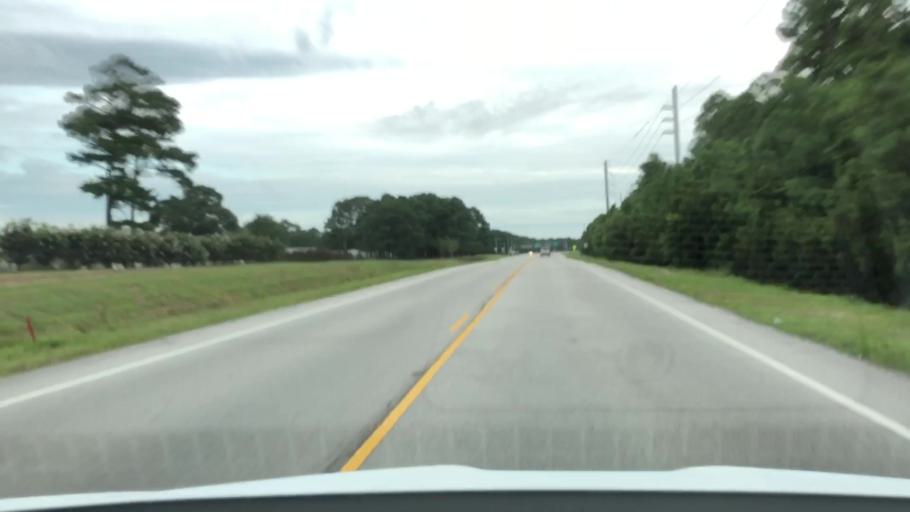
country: US
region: North Carolina
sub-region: Carteret County
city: Cedar Point
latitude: 34.6825
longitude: -77.0679
